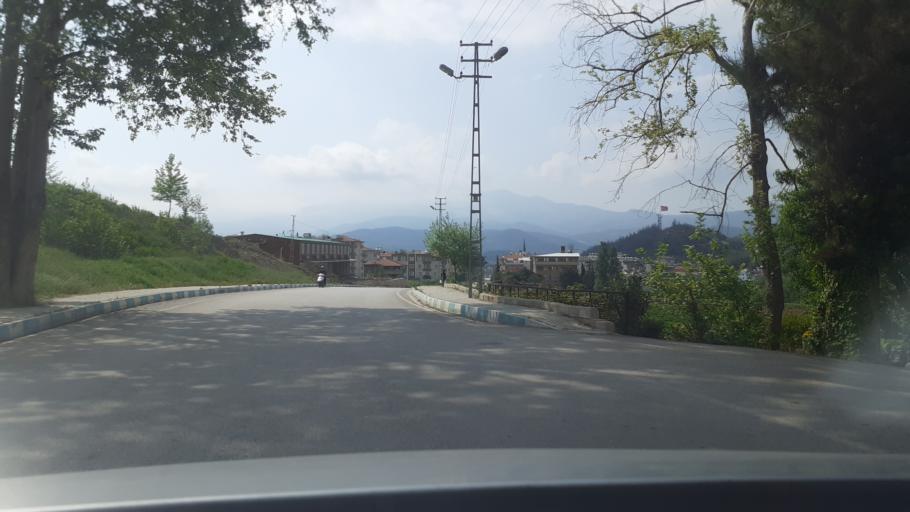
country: TR
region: Hatay
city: Yayladagi
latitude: 35.8978
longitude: 36.0750
